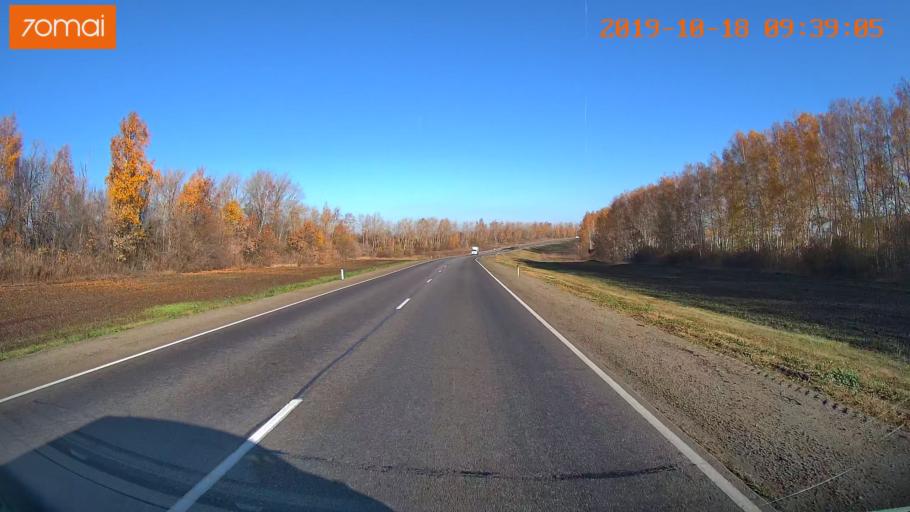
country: RU
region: Tula
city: Yefremov
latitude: 53.2478
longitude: 38.1344
